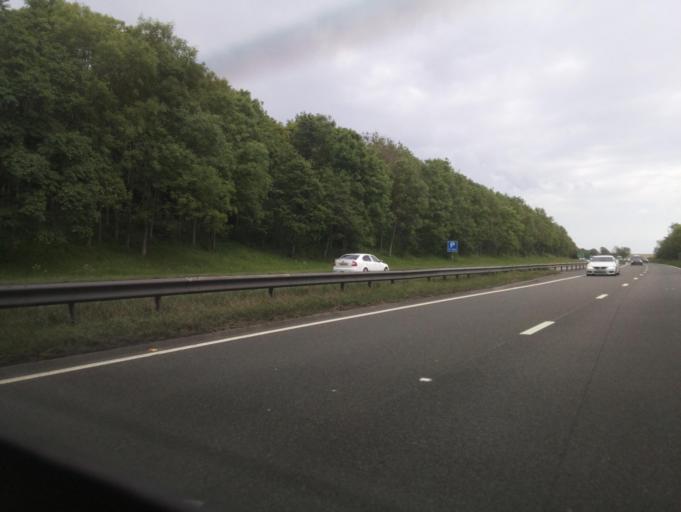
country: GB
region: England
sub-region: County Durham
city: Houghton-le-Spring
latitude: 54.8618
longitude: -1.4414
